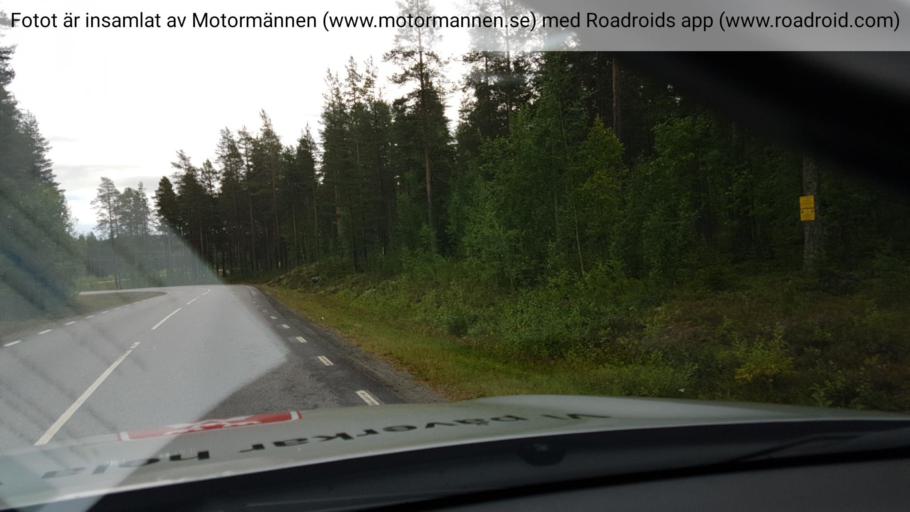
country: SE
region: Norrbotten
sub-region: Bodens Kommun
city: Boden
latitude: 65.7982
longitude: 21.6579
